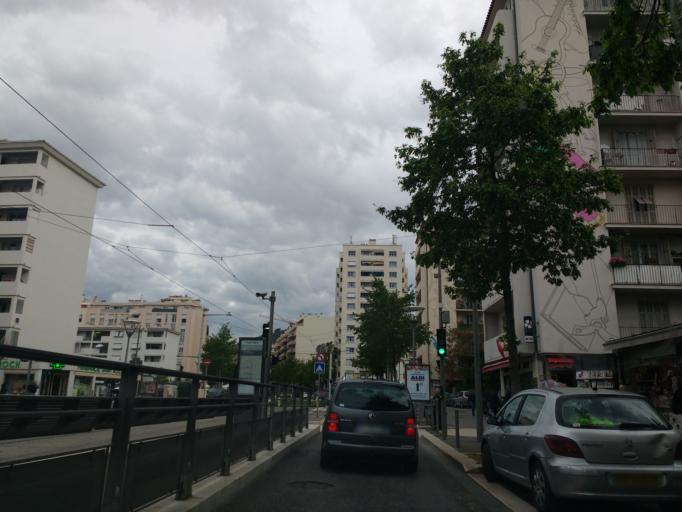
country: FR
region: Provence-Alpes-Cote d'Azur
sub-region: Departement des Alpes-Maritimes
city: Villefranche-sur-Mer
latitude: 43.7150
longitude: 7.2929
